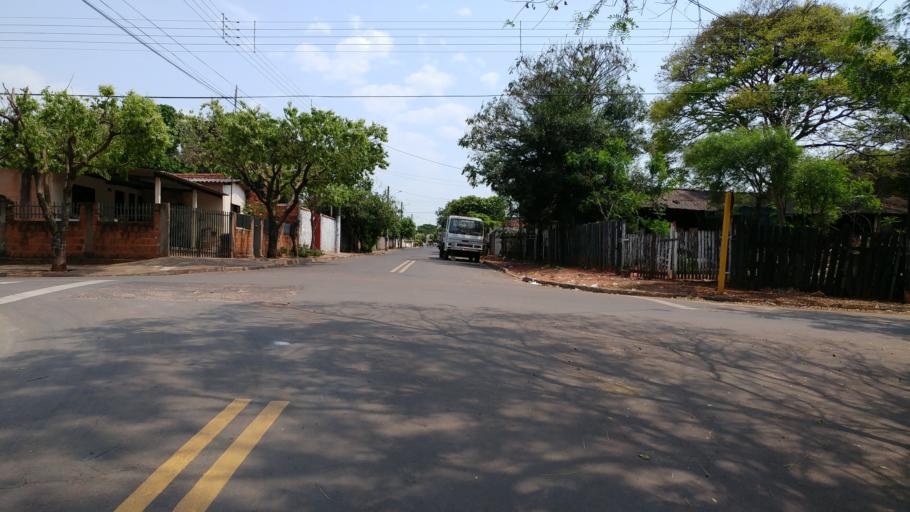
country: BR
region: Sao Paulo
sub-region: Paraguacu Paulista
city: Paraguacu Paulista
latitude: -22.4162
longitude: -50.5673
